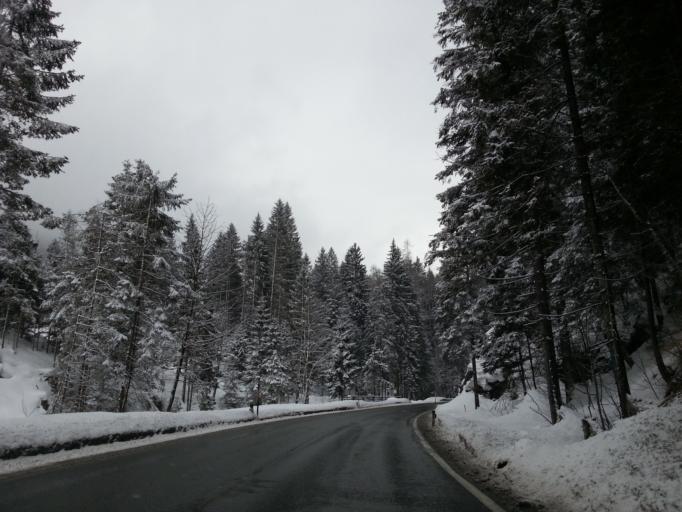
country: AT
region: Salzburg
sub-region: Politischer Bezirk Sankt Johann im Pongau
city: Eben im Pongau
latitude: 47.4766
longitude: 13.3913
